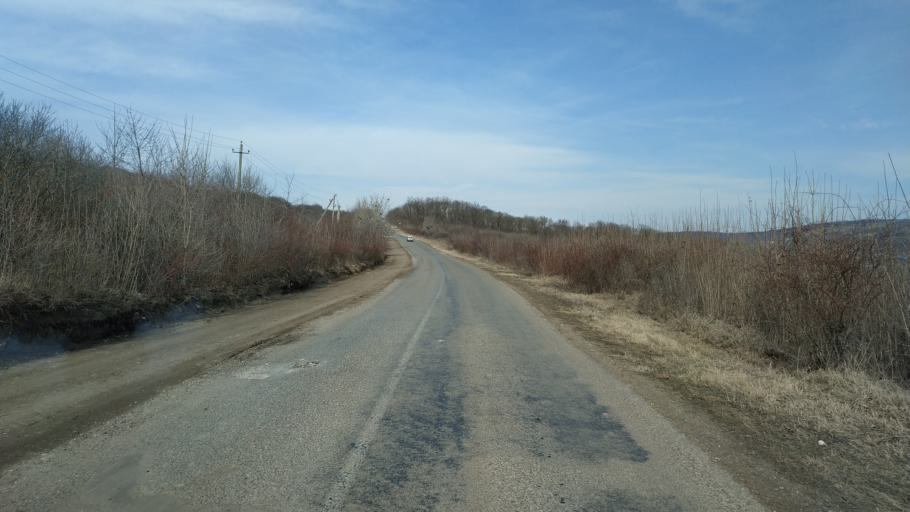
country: MD
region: Nisporeni
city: Nisporeni
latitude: 47.1872
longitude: 28.0713
